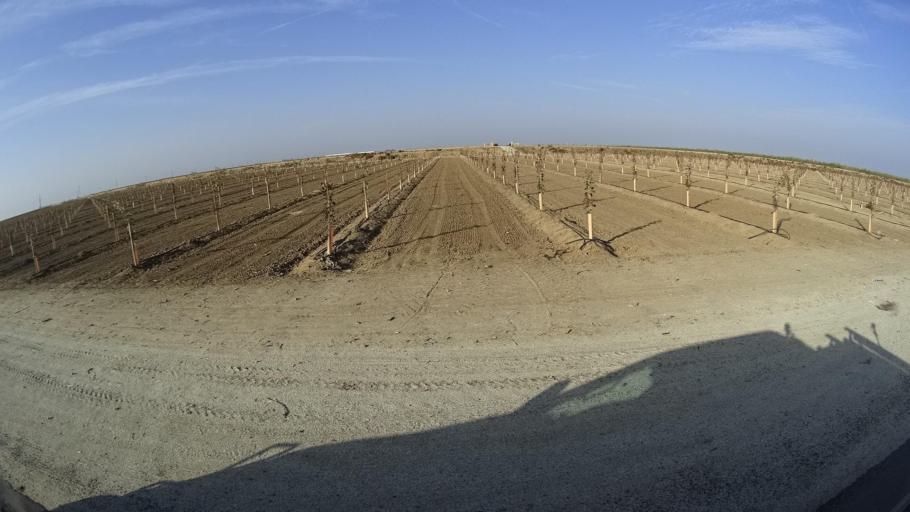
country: US
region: California
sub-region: Kern County
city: McFarland
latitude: 35.7082
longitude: -119.1872
